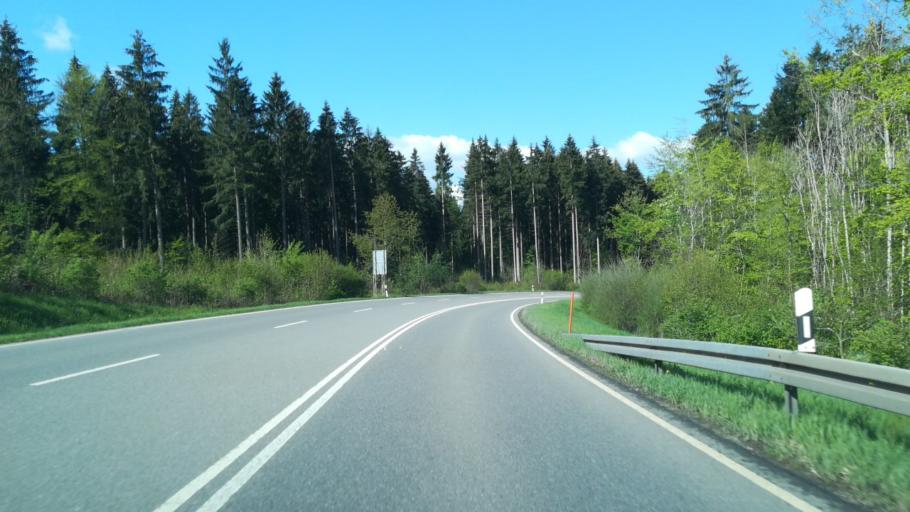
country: DE
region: Baden-Wuerttemberg
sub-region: Freiburg Region
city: Blumberg
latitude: 47.8222
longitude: 8.5665
